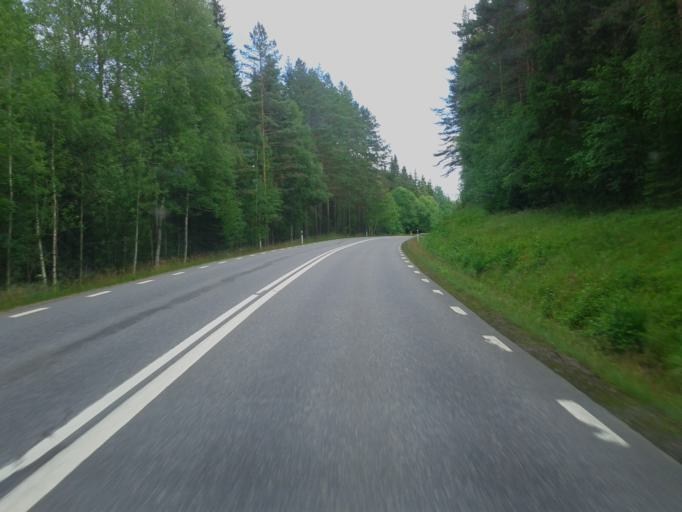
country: SE
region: Dalarna
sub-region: Faluns Kommun
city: Bjursas
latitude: 60.7400
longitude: 15.4260
